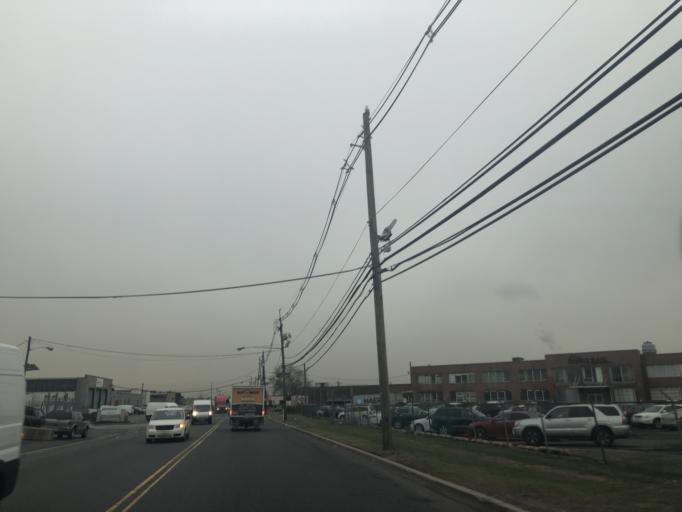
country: US
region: New Jersey
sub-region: Union County
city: Elizabeth
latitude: 40.6723
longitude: -74.1901
